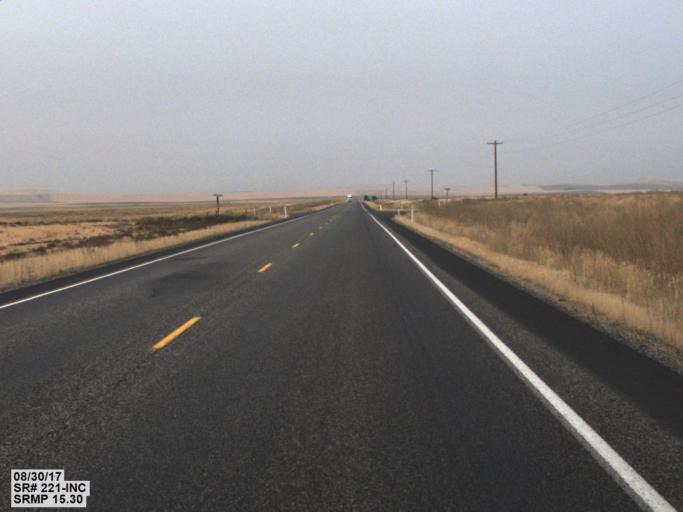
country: US
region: Washington
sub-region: Benton County
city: Benton City
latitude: 46.1567
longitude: -119.6010
